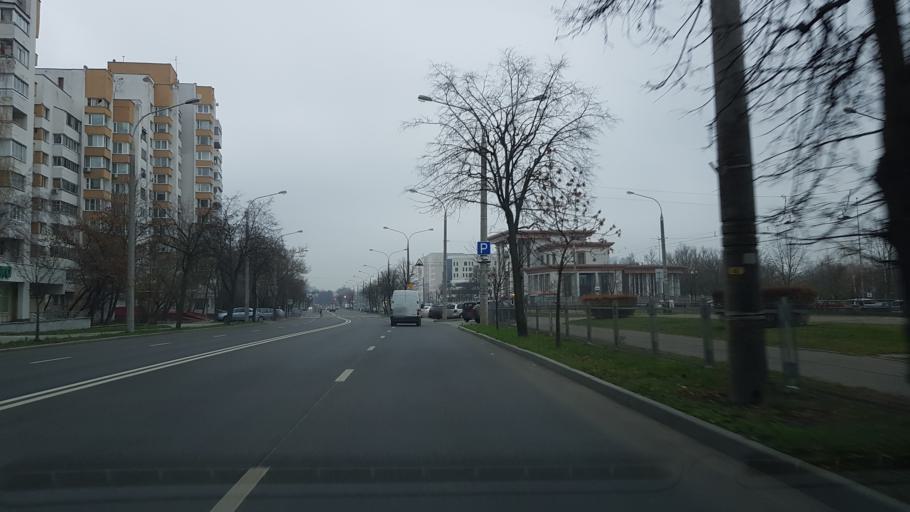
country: BY
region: Minsk
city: Minsk
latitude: 53.9258
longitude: 27.5453
